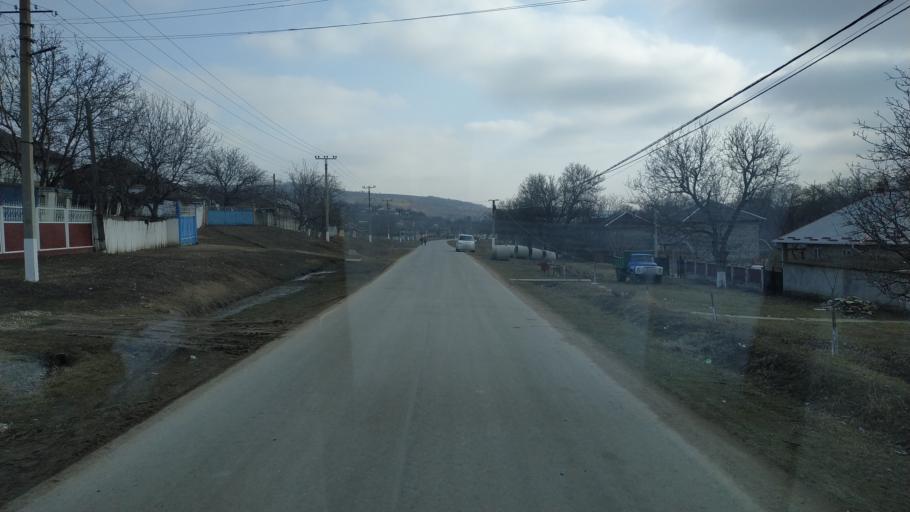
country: MD
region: Nisporeni
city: Nisporeni
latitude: 46.9411
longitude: 28.3256
